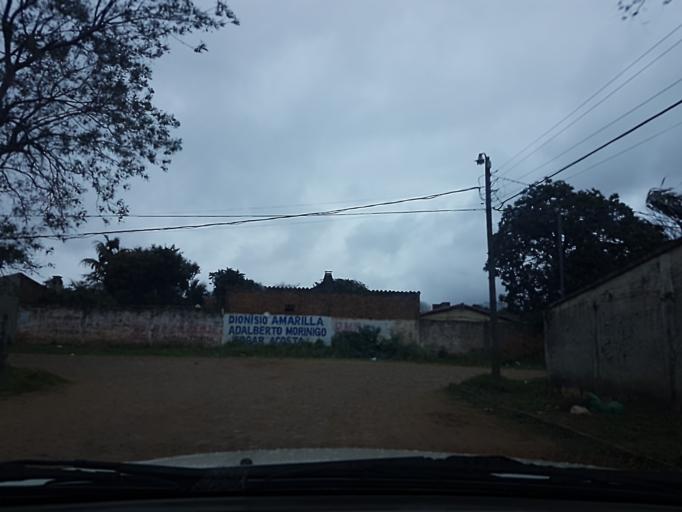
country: PY
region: Central
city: Colonia Mariano Roque Alonso
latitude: -25.2108
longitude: -57.5241
